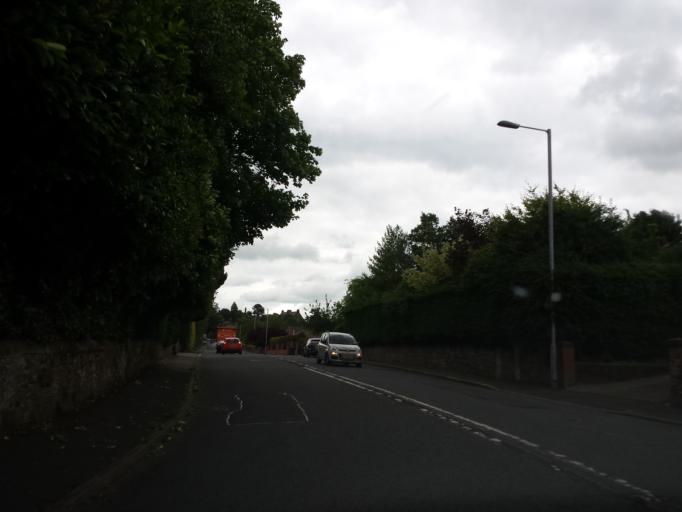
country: GB
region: Scotland
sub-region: Dumfries and Galloway
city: Dumfries
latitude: 55.0645
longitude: -3.6299
